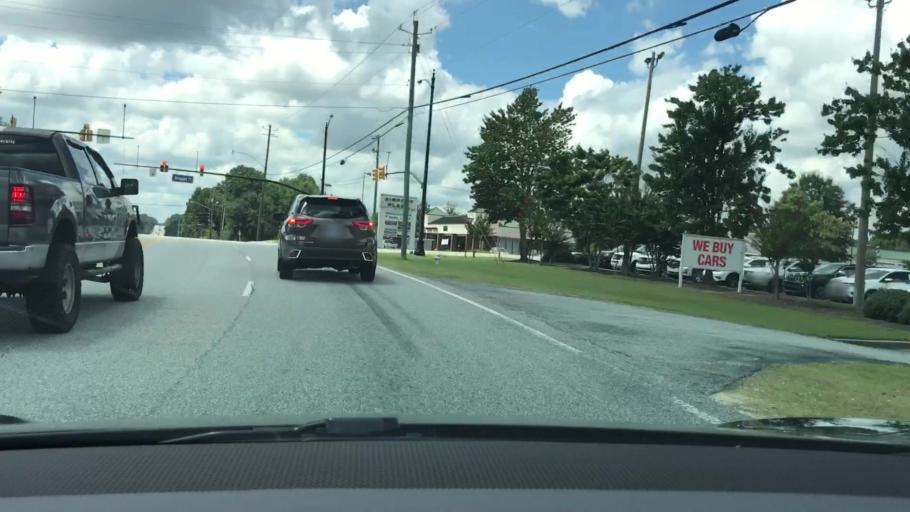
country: US
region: Alabama
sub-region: Lee County
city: Auburn
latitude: 32.6089
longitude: -85.4429
